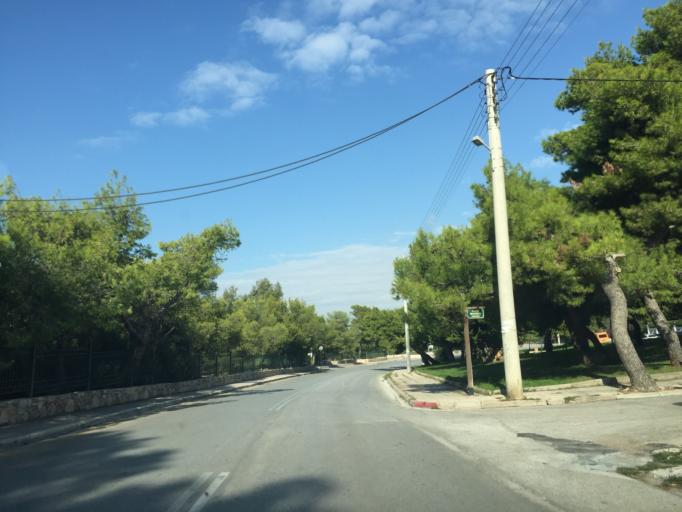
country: GR
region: Attica
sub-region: Nomarchia Anatolikis Attikis
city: Vouliagmeni
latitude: 37.8182
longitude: 23.7713
